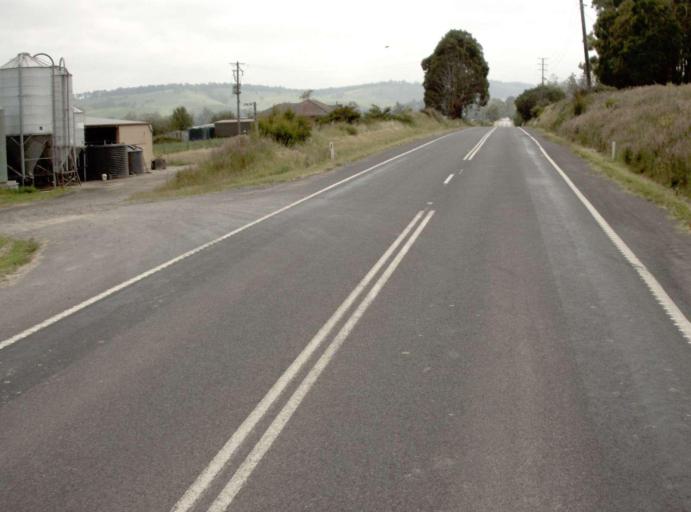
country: AU
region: Victoria
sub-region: Baw Baw
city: Warragul
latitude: -38.4223
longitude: 146.0403
